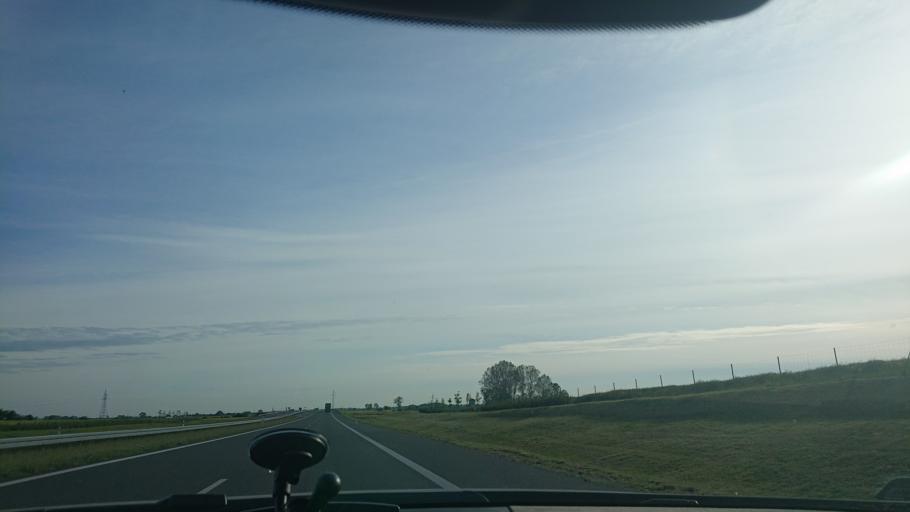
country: PL
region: Greater Poland Voivodeship
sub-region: Powiat gnieznienski
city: Gniezno
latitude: 52.5370
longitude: 17.5219
